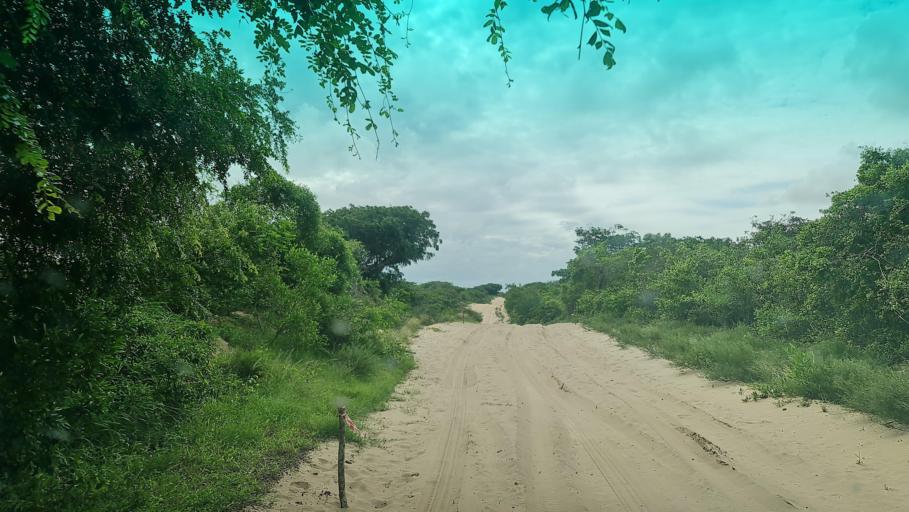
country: MZ
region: Maputo
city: Manhica
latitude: -25.4368
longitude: 32.9151
